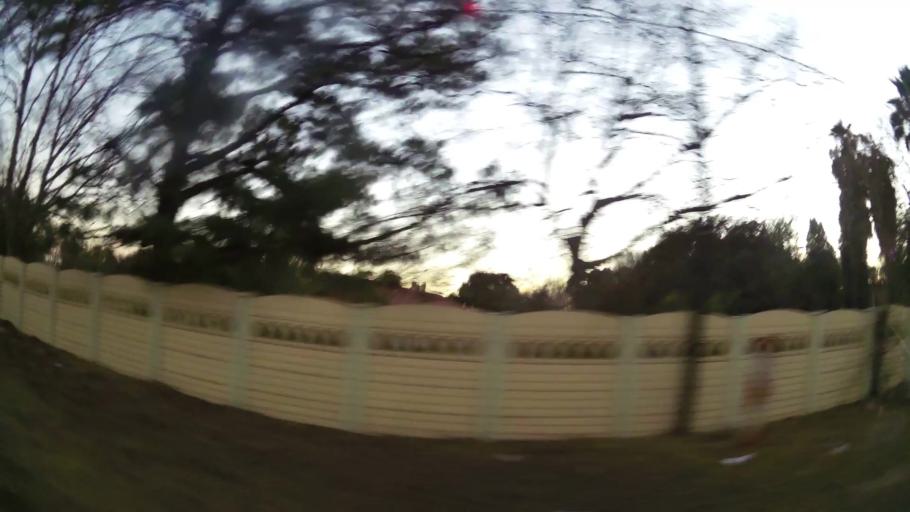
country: ZA
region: Gauteng
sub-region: City of Tshwane Metropolitan Municipality
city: Centurion
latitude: -25.8540
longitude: 28.1334
